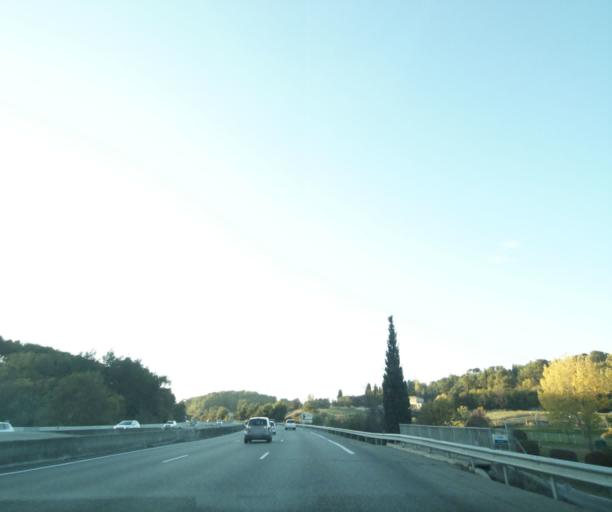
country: FR
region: Provence-Alpes-Cote d'Azur
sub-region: Departement des Bouches-du-Rhone
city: Le Tholonet
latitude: 43.5123
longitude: 5.4946
